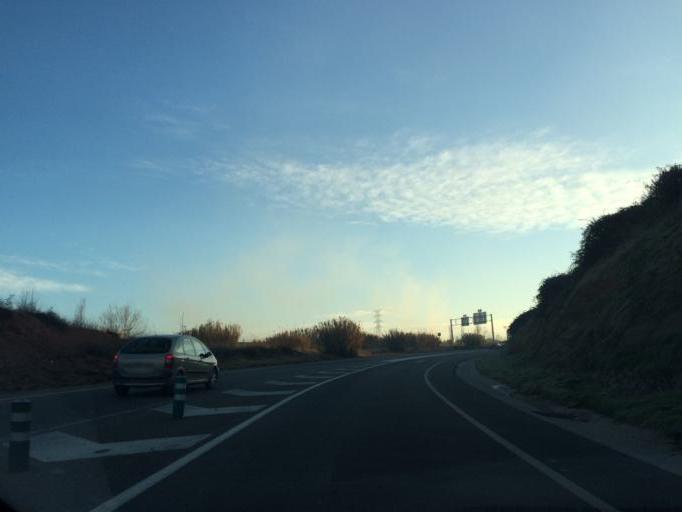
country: ES
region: Catalonia
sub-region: Provincia de Barcelona
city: Manresa
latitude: 41.7444
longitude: 1.8305
